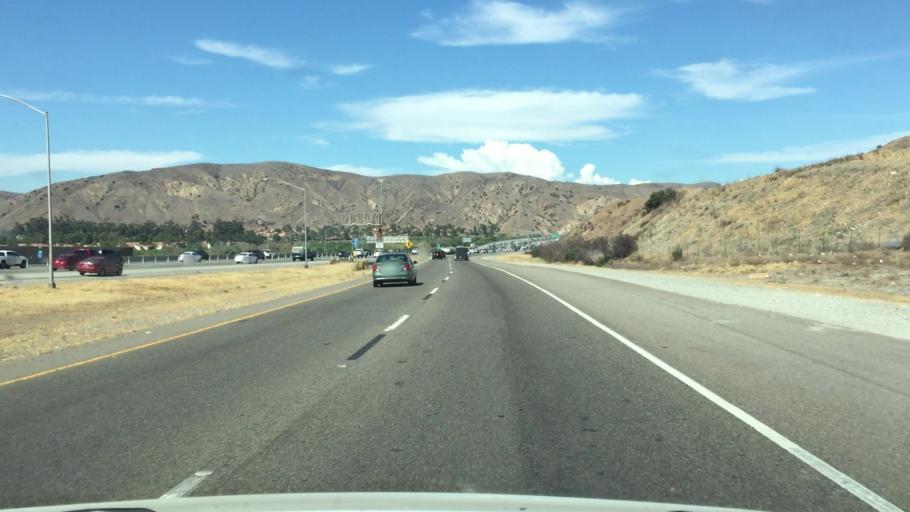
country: US
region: California
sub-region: San Bernardino County
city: Los Serranos
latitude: 33.8682
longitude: -117.7069
